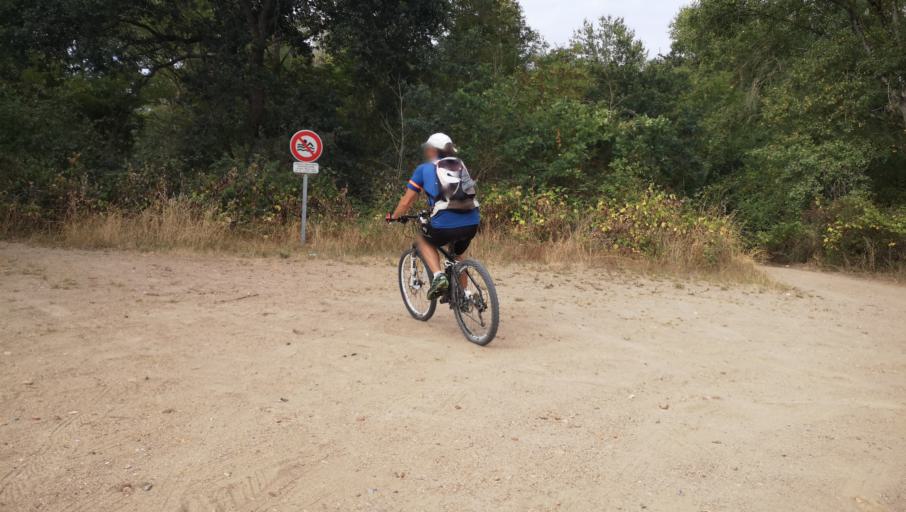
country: FR
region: Centre
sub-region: Departement du Loiret
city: Sandillon
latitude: 47.8592
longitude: 2.0352
